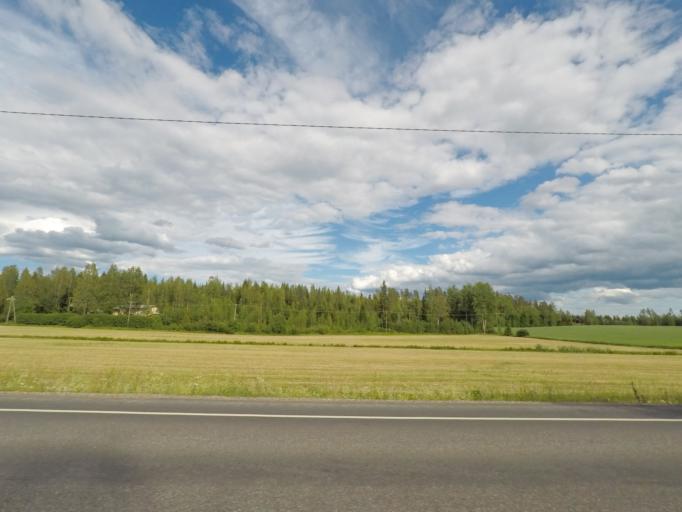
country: FI
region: Uusimaa
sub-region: Porvoo
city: Pukkila
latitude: 60.7748
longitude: 25.4529
